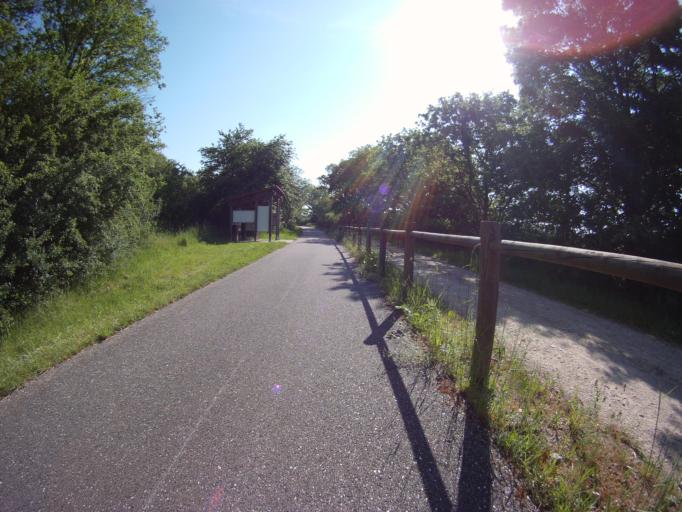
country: FR
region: Lorraine
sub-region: Departement de Meurthe-et-Moselle
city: Champenoux
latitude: 48.7398
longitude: 6.3124
